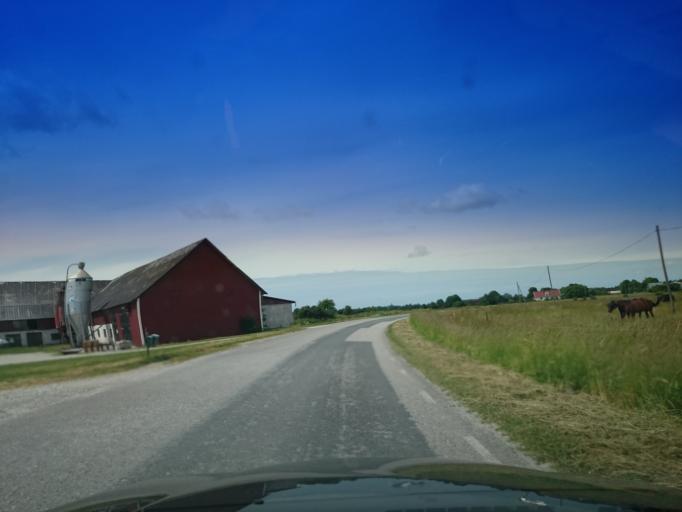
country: SE
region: Gotland
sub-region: Gotland
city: Hemse
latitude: 57.2479
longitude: 18.5538
